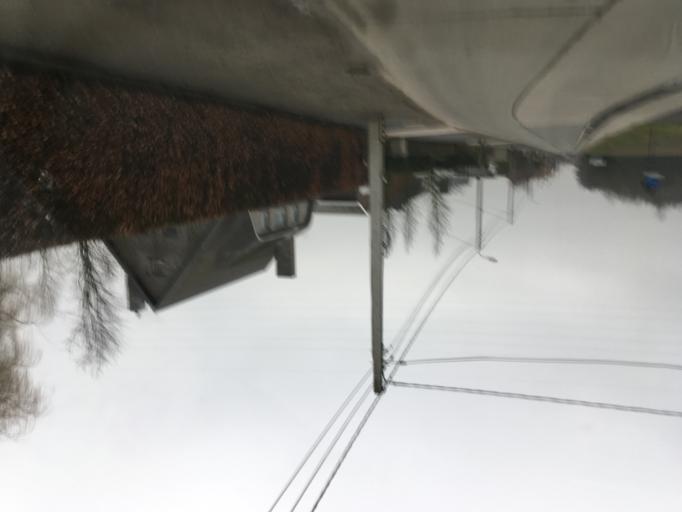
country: BE
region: Flanders
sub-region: Provincie West-Vlaanderen
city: Izegem
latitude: 50.9054
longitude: 3.1603
